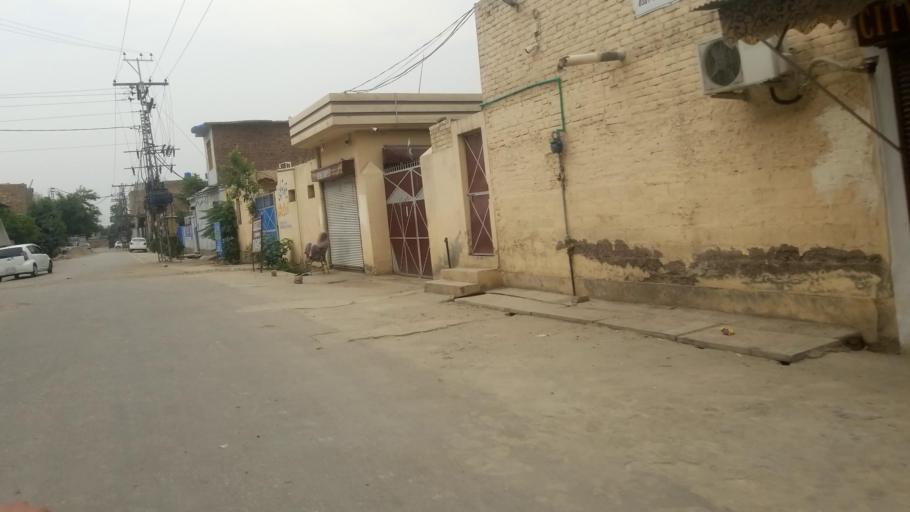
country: PK
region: Khyber Pakhtunkhwa
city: Peshawar
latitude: 33.9818
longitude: 71.5581
